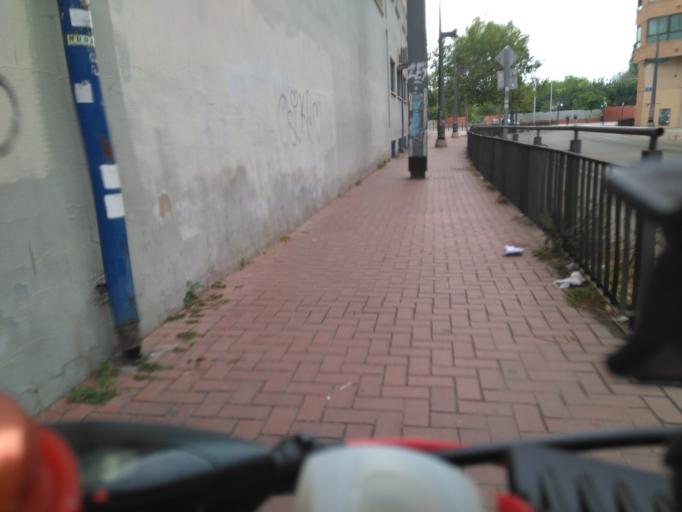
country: ES
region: Valencia
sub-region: Provincia de Valencia
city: Valencia
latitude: 39.4889
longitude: -0.3846
